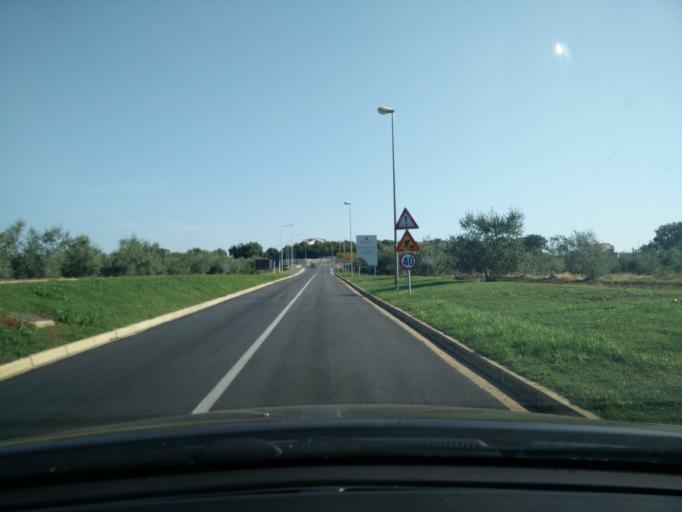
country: HR
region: Istarska
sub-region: Grad Porec
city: Porec
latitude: 45.2028
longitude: 13.6015
